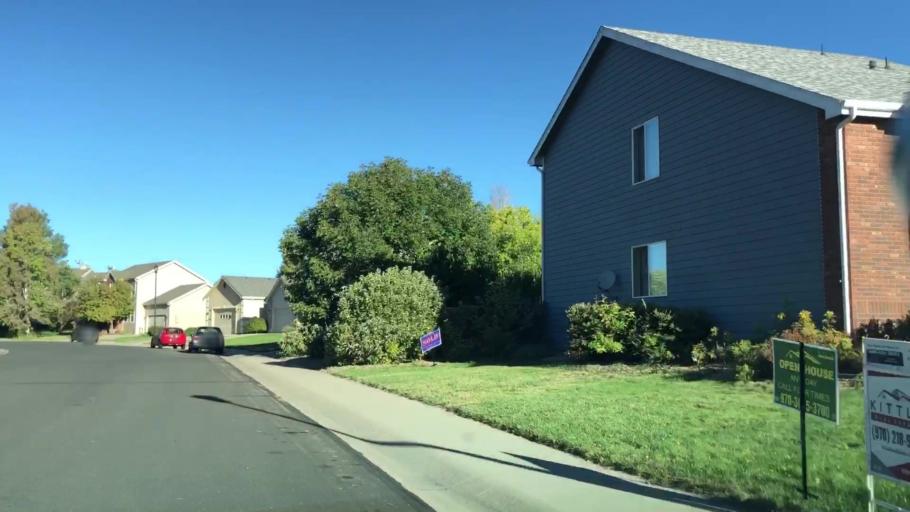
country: US
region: Colorado
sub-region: Larimer County
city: Fort Collins
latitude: 40.5181
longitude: -105.0351
